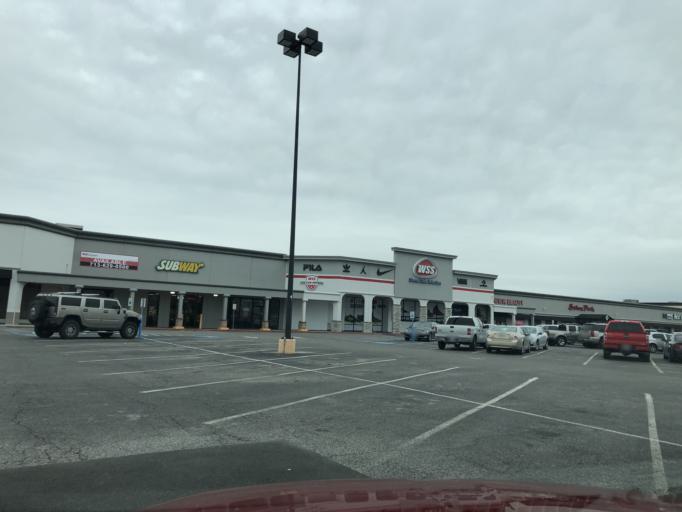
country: US
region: Texas
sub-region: Harris County
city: Spring Valley
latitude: 29.8198
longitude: -95.4670
